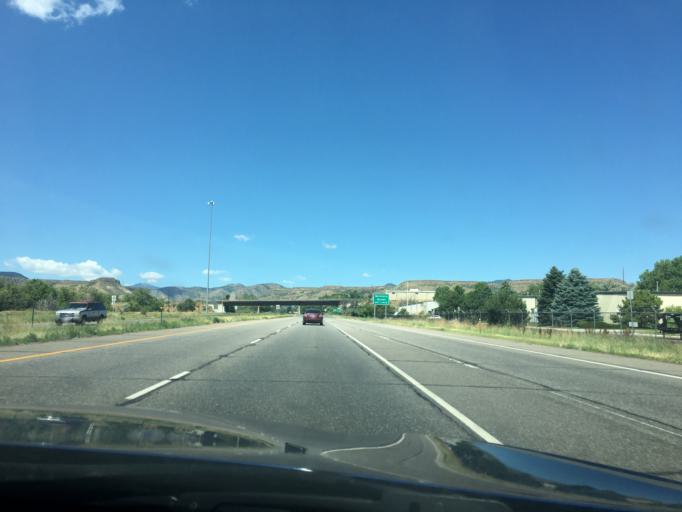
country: US
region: Colorado
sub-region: Jefferson County
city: Applewood
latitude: 39.7753
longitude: -105.1521
